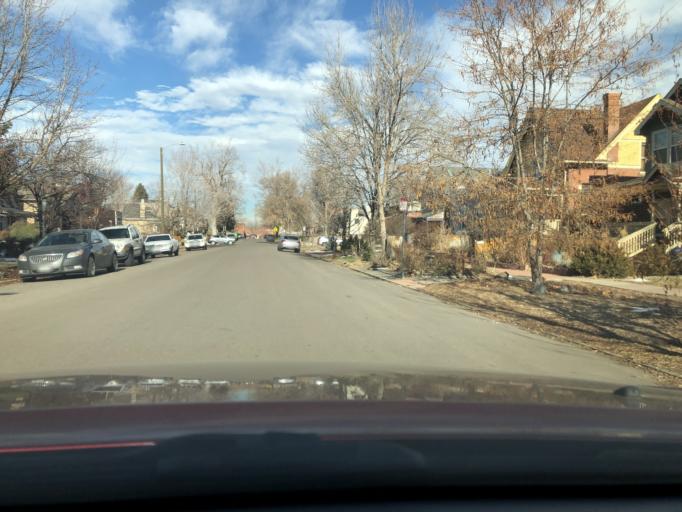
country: US
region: Colorado
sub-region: Denver County
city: Denver
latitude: 39.7524
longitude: -104.9672
